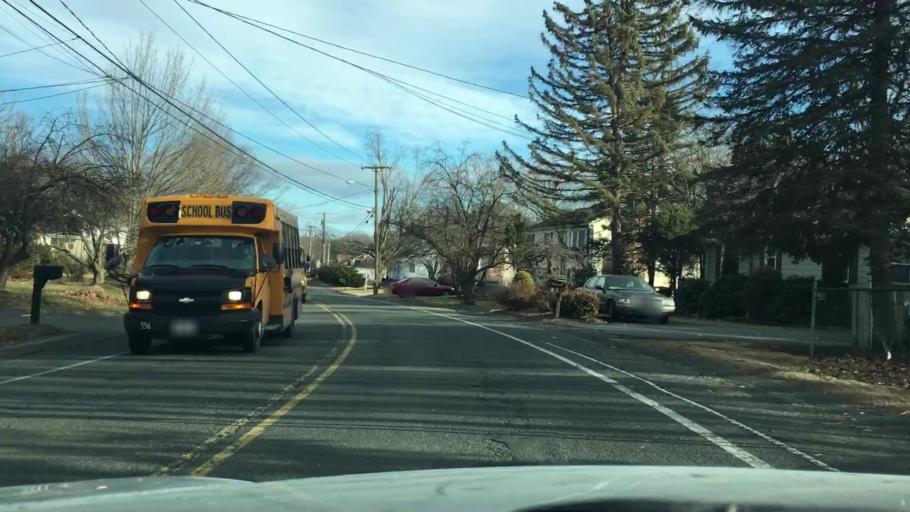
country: US
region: Massachusetts
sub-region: Hampden County
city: Agawam
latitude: 42.0674
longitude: -72.6341
